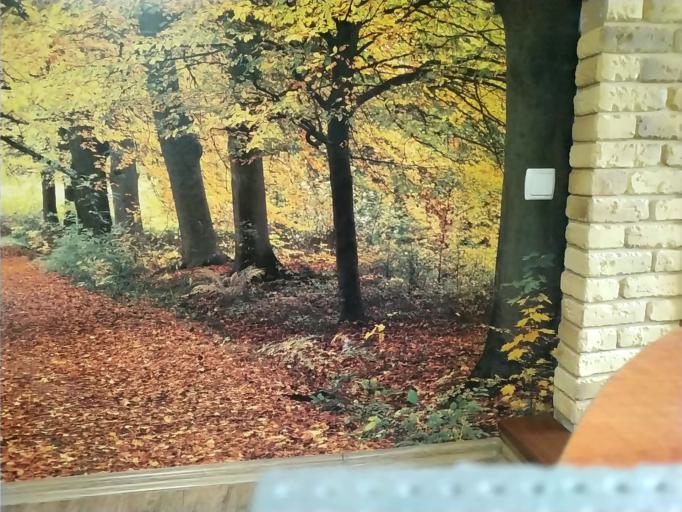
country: RU
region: Tverskaya
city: Staritsa
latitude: 56.5392
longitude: 34.9777
